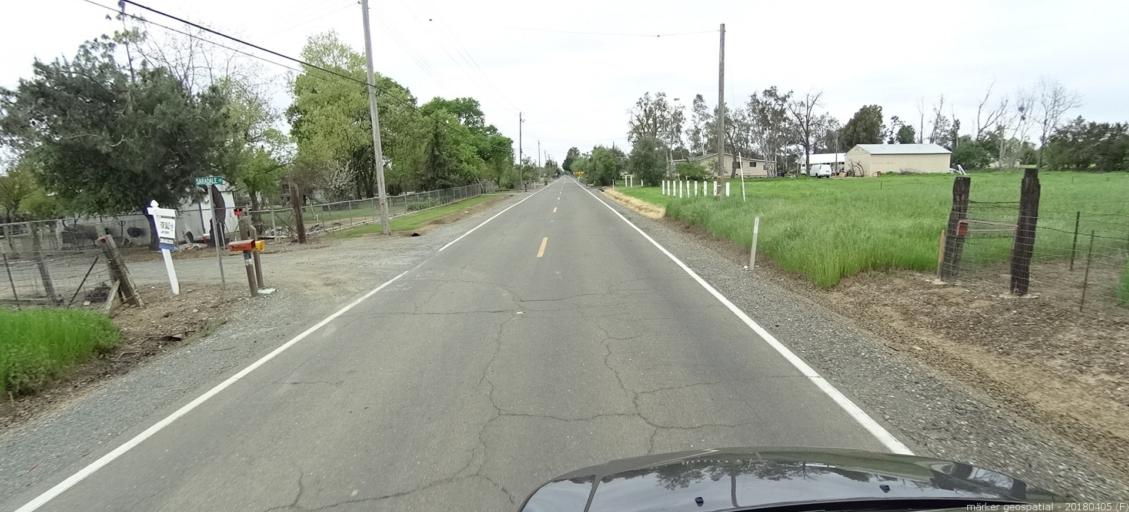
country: US
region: California
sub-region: Sacramento County
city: Galt
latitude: 38.2474
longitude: -121.3231
